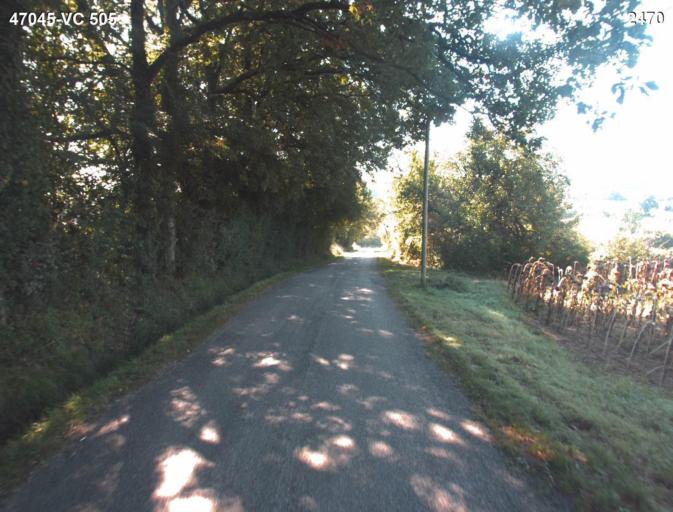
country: FR
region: Aquitaine
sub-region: Departement du Lot-et-Garonne
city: Nerac
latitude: 44.1428
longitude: 0.4159
